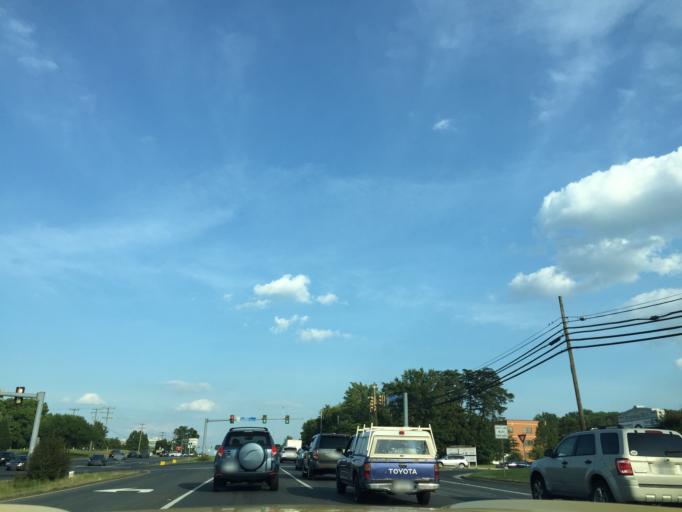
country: US
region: Virginia
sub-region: Loudoun County
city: Countryside
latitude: 39.0270
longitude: -77.3956
